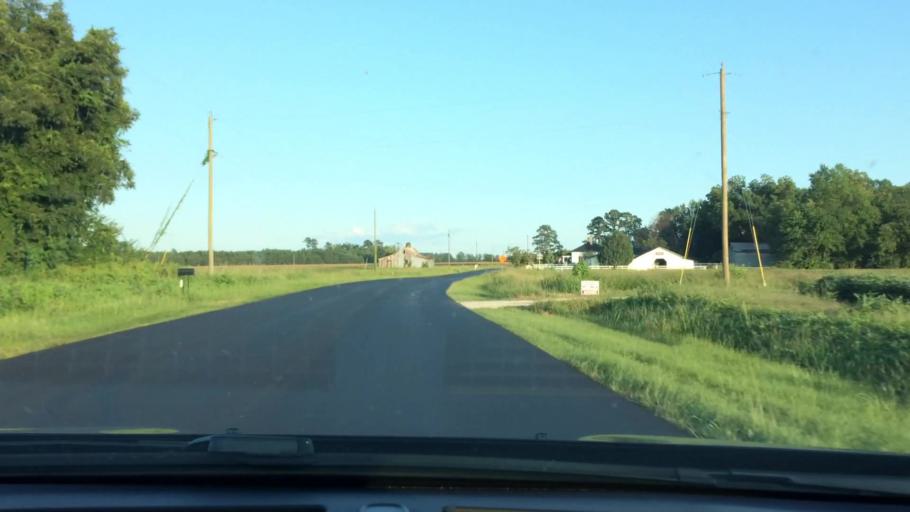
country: US
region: North Carolina
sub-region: Pitt County
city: Ayden
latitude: 35.4471
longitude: -77.4606
